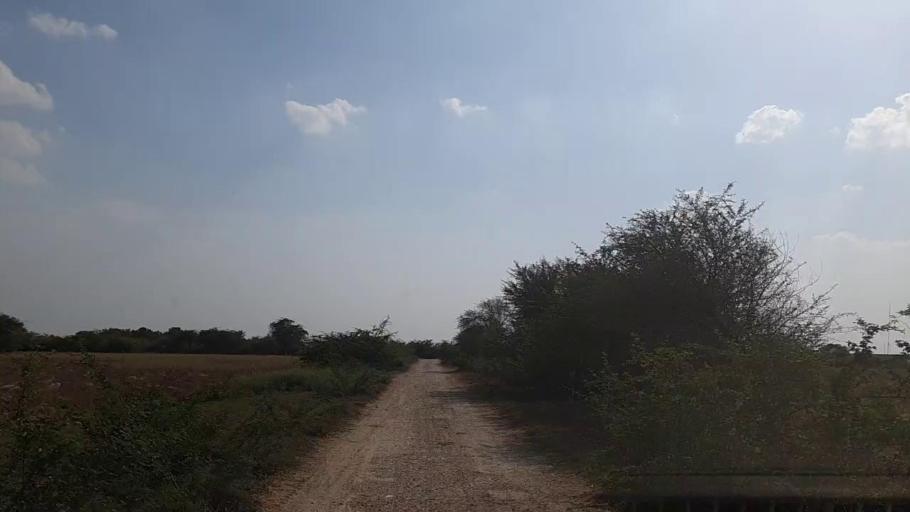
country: PK
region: Sindh
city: Jati
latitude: 24.4797
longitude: 68.3393
